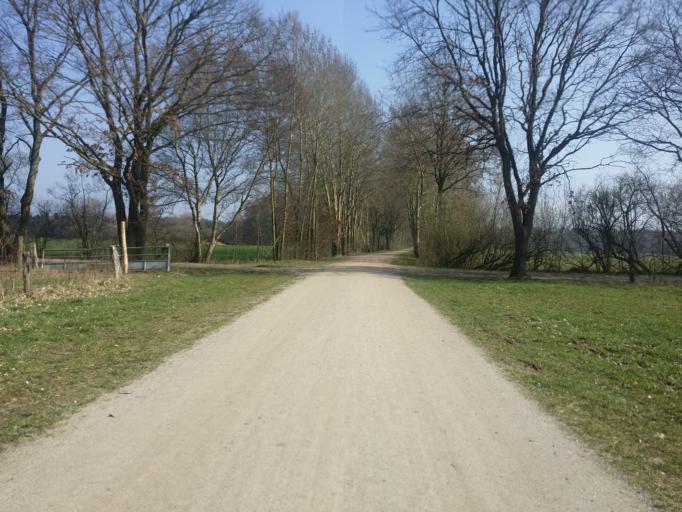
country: DE
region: Lower Saxony
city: Delmenhorst
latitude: 53.0146
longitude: 8.6681
